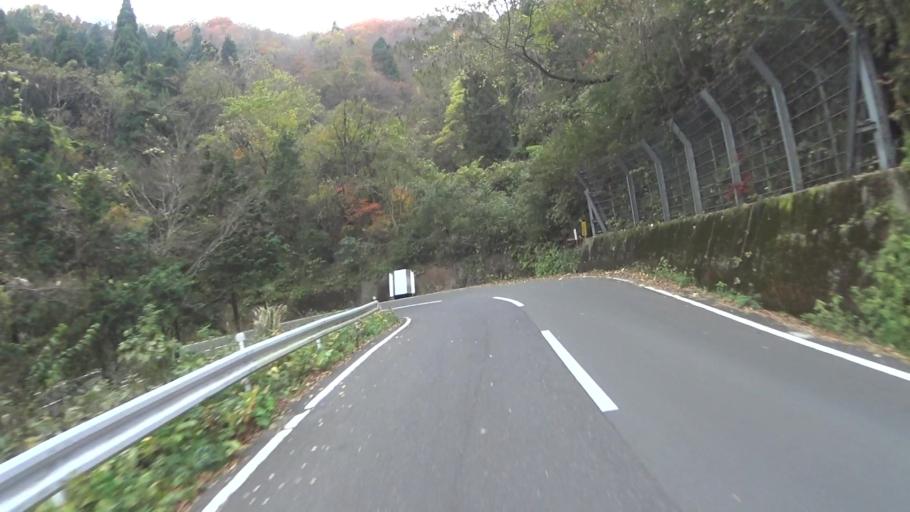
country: JP
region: Kyoto
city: Maizuru
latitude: 35.5399
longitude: 135.4485
